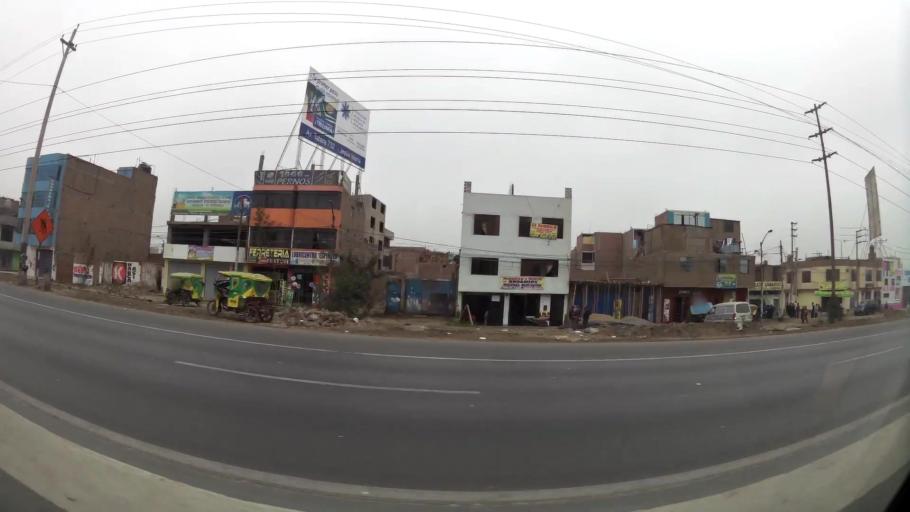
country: PE
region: Lima
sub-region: Lima
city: Urb. Santo Domingo
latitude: -11.8934
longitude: -77.0681
